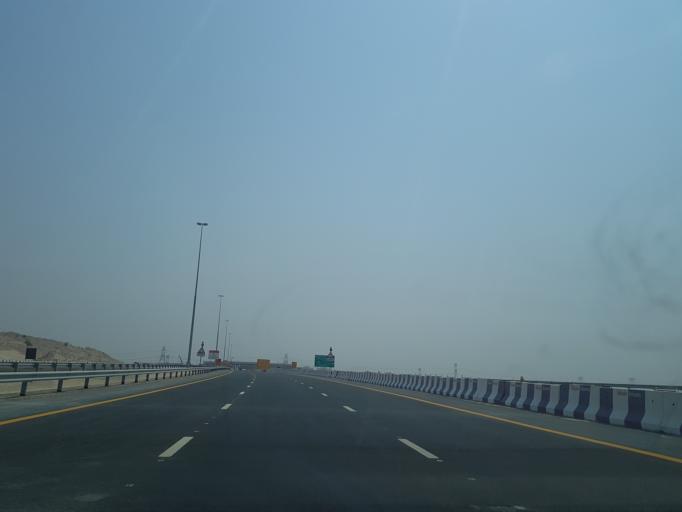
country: AE
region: Dubai
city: Dubai
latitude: 25.0008
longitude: 55.1885
